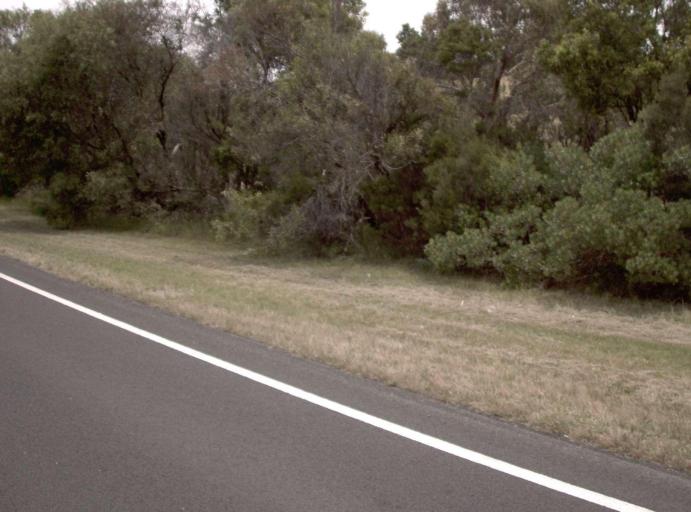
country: AU
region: Victoria
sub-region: Mornington Peninsula
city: Mount Martha
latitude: -38.2869
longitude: 145.0500
